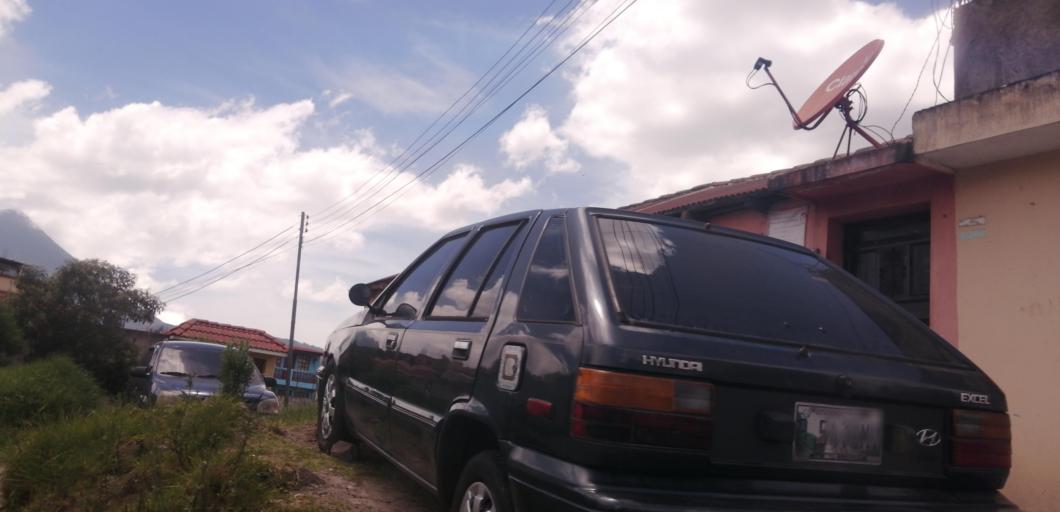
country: GT
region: Quetzaltenango
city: Quetzaltenango
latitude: 14.8308
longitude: -91.5350
